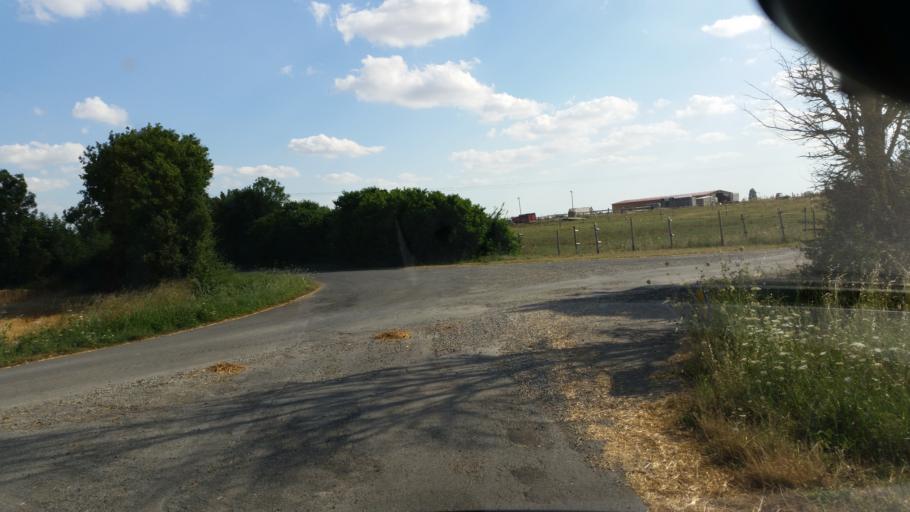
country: FR
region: Poitou-Charentes
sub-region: Departement de la Charente-Maritime
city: Saint-Jean-de-Liversay
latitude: 46.2306
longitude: -0.8888
